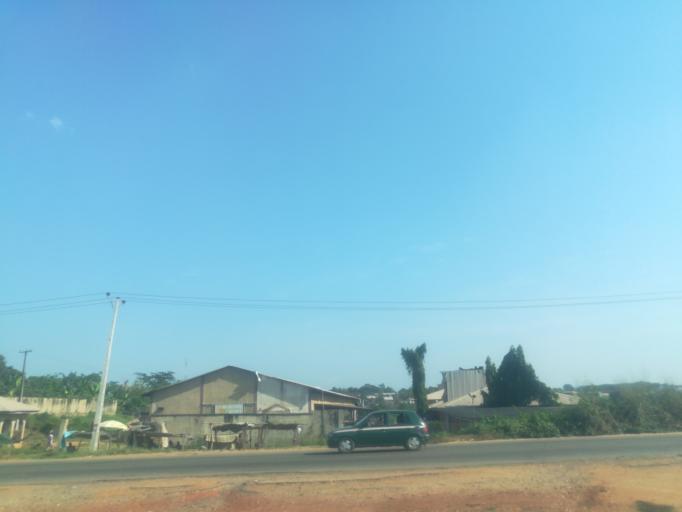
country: NG
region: Ogun
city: Abeokuta
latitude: 7.1492
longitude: 3.3205
